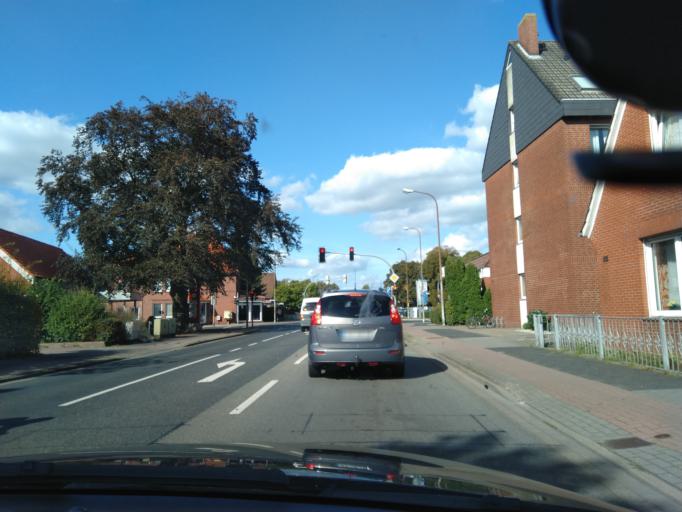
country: DE
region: Lower Saxony
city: Leer
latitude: 53.2432
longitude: 7.4569
